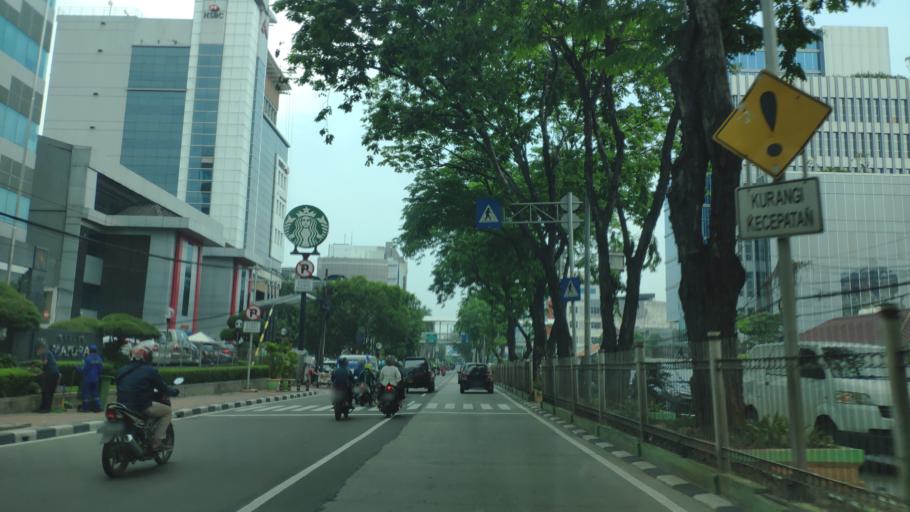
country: ID
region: Jakarta Raya
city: Jakarta
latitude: -6.1778
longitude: 106.7991
